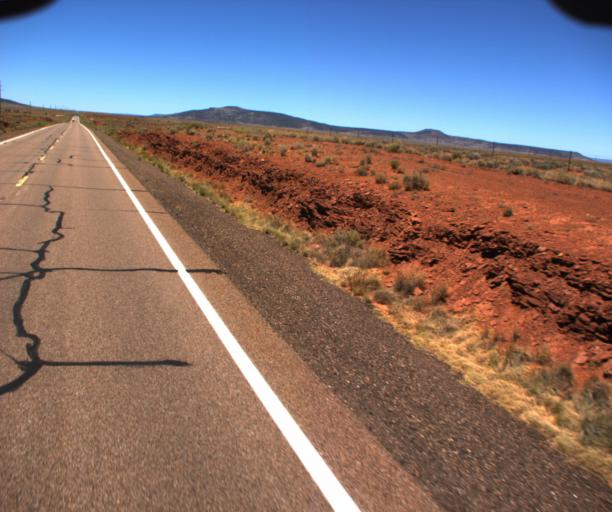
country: US
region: Arizona
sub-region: Coconino County
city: LeChee
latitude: 34.9135
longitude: -110.8321
